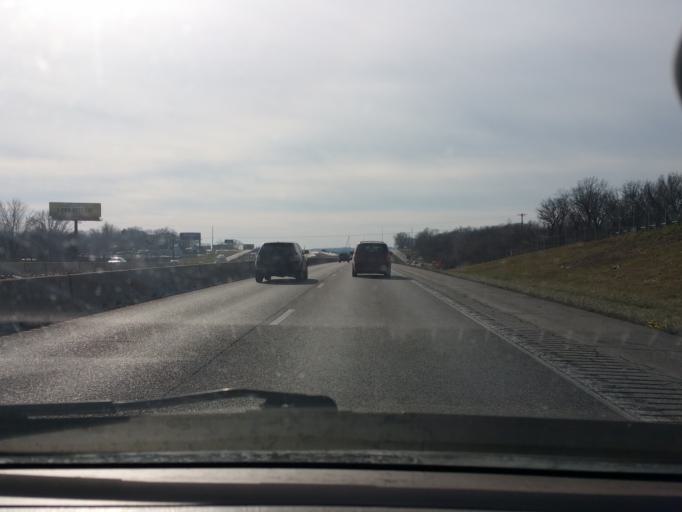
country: US
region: Missouri
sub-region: Clay County
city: Pleasant Valley
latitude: 39.2251
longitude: -94.4696
